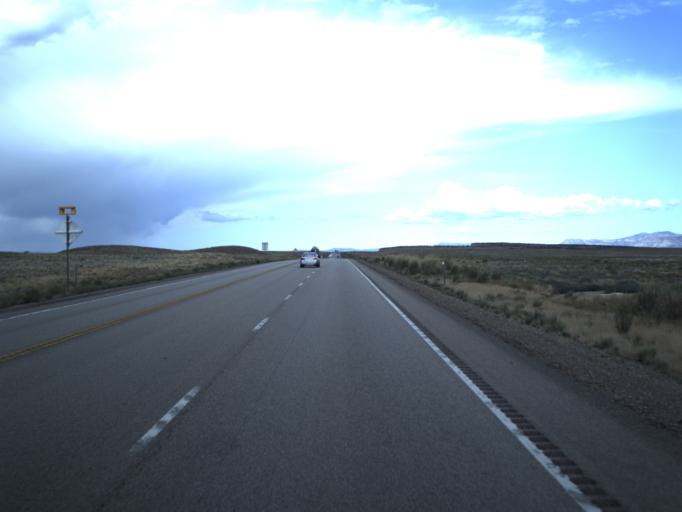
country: US
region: Utah
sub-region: Carbon County
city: Wellington
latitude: 39.5279
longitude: -110.5782
